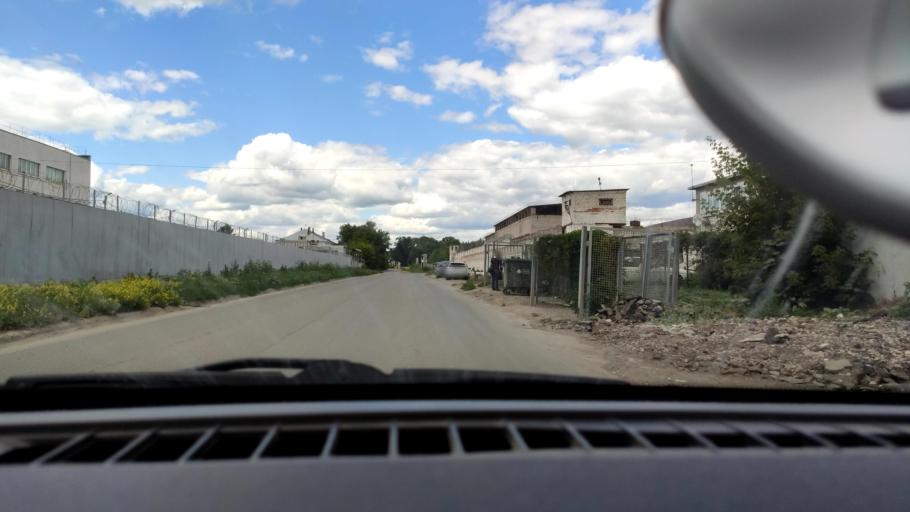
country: RU
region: Samara
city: Samara
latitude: 53.1917
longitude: 50.2650
